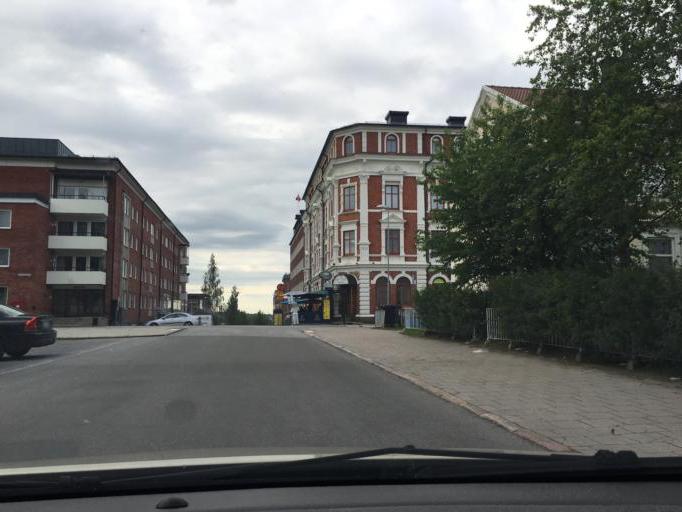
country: SE
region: Norrbotten
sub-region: Lulea Kommun
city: Lulea
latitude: 65.5829
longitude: 22.1504
